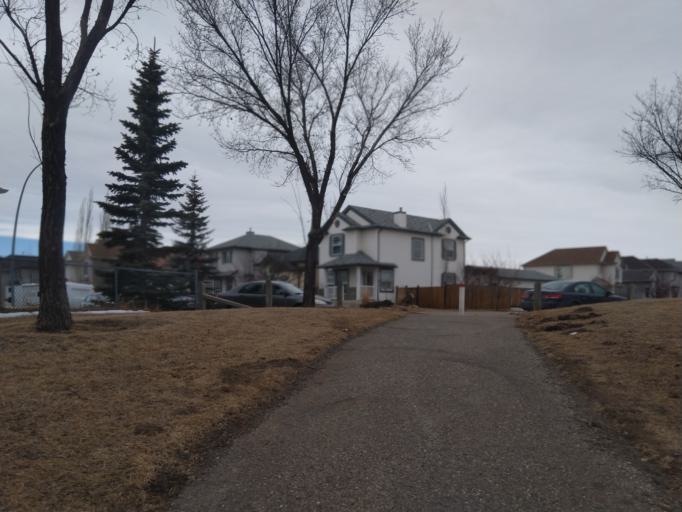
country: CA
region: Alberta
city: Calgary
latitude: 51.1686
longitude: -114.0444
